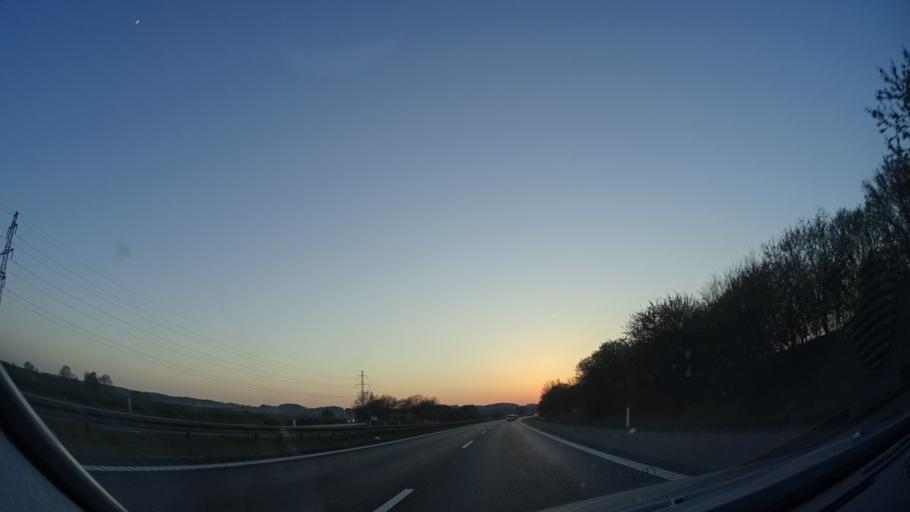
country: DK
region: Zealand
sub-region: Lejre Kommune
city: Lejre
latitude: 55.6223
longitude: 11.9839
